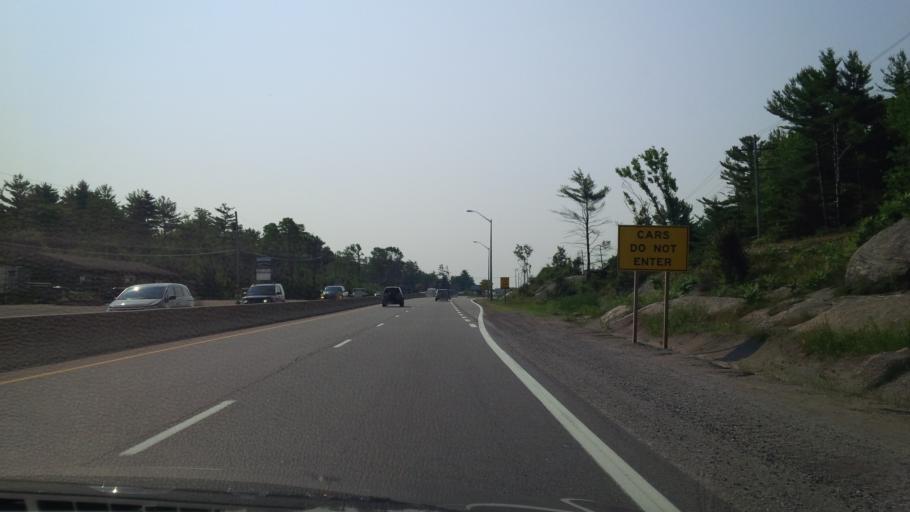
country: CA
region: Ontario
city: Gravenhurst
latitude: 44.8897
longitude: -79.3529
